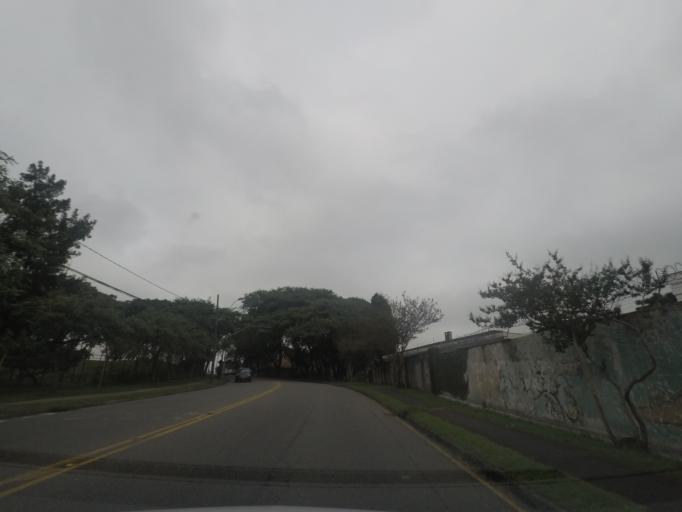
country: BR
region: Parana
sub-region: Curitiba
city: Curitiba
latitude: -25.4424
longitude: -49.2421
